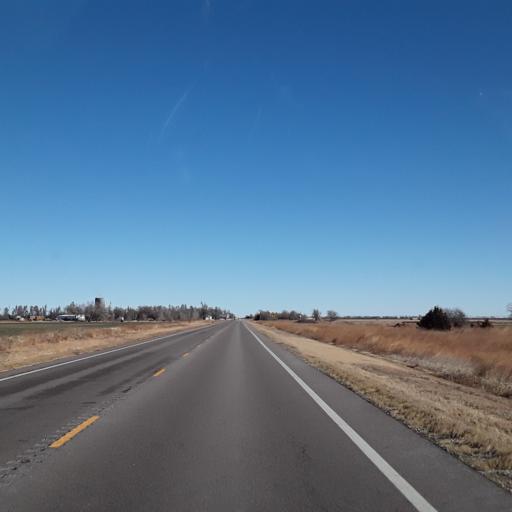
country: US
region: Kansas
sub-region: Pawnee County
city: Larned
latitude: 38.1124
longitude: -99.1901
